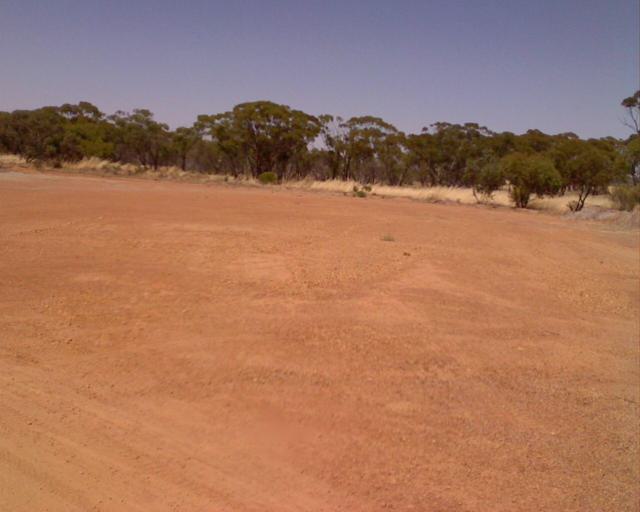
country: AU
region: Western Australia
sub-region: Merredin
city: Merredin
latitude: -31.6070
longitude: 117.8752
